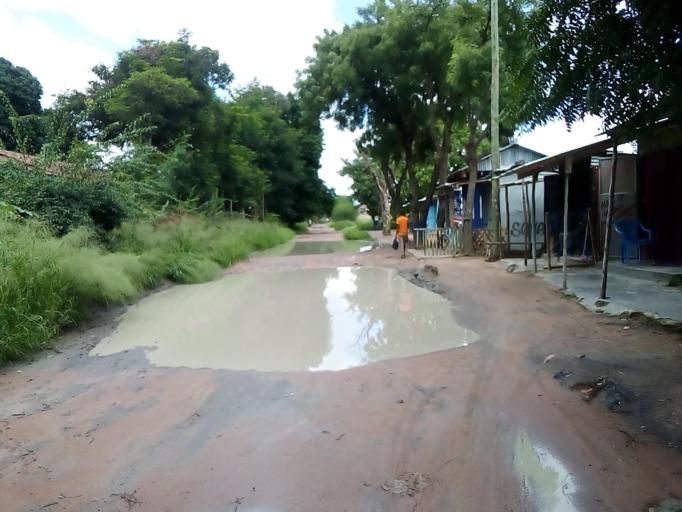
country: TZ
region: Dodoma
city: Dodoma
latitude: -6.1208
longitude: 35.7440
